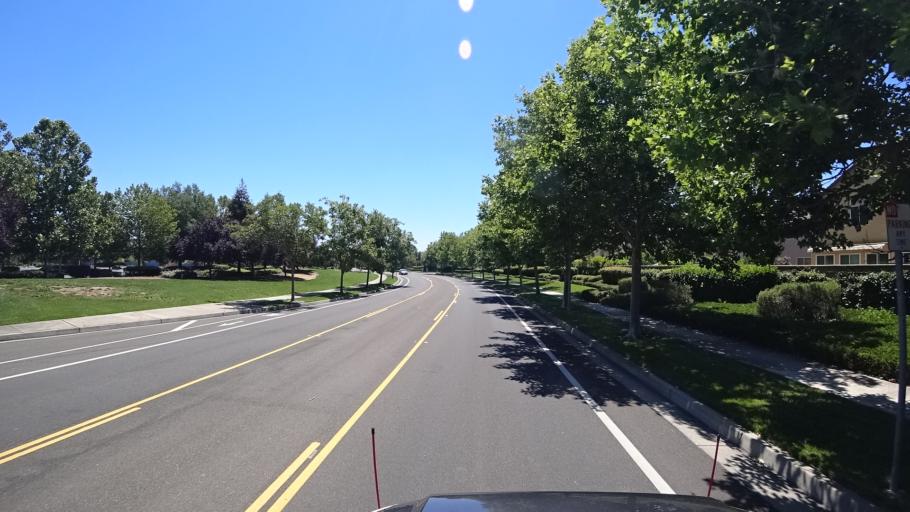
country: US
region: California
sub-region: Yolo County
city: West Sacramento
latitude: 38.6485
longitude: -121.5318
